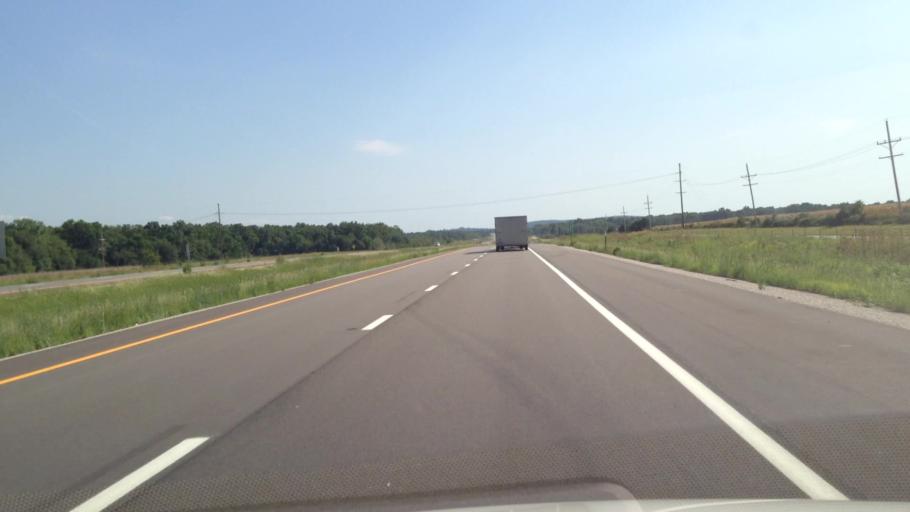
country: US
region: Kansas
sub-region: Linn County
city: La Cygne
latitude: 38.3261
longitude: -94.6778
